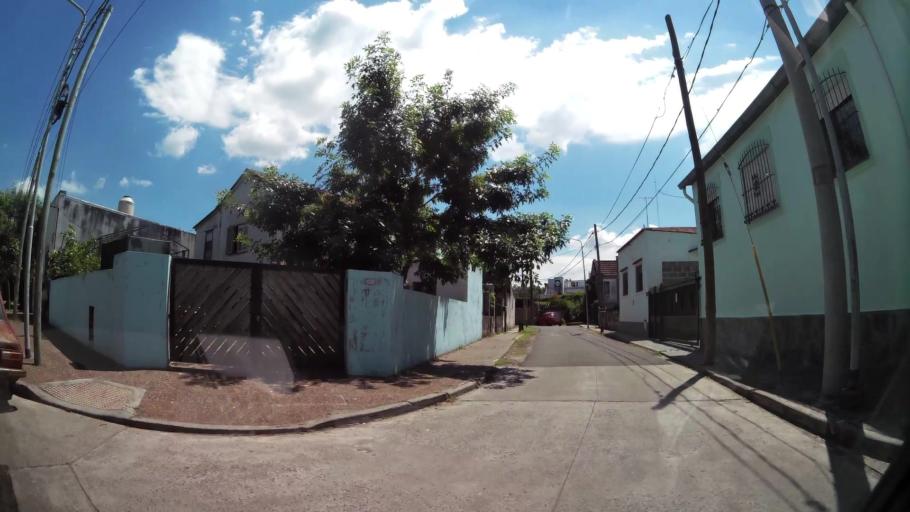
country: AR
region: Buenos Aires
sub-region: Partido de Tigre
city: Tigre
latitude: -34.4299
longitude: -58.5736
